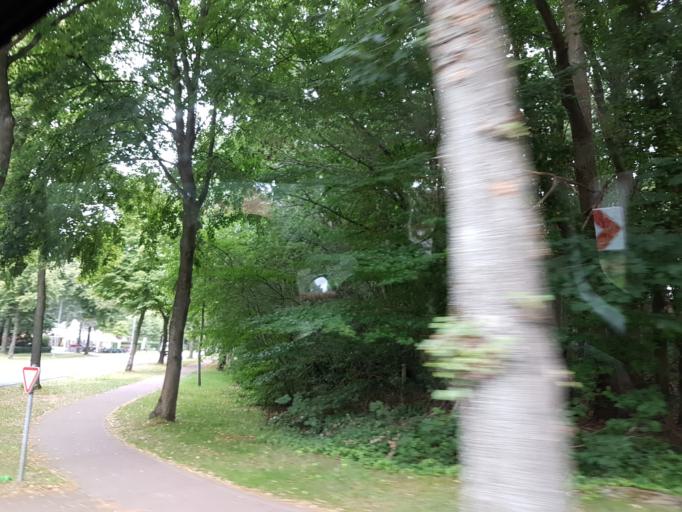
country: BE
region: Flanders
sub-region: Provincie Antwerpen
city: Westerlo
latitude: 51.0985
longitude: 4.9092
